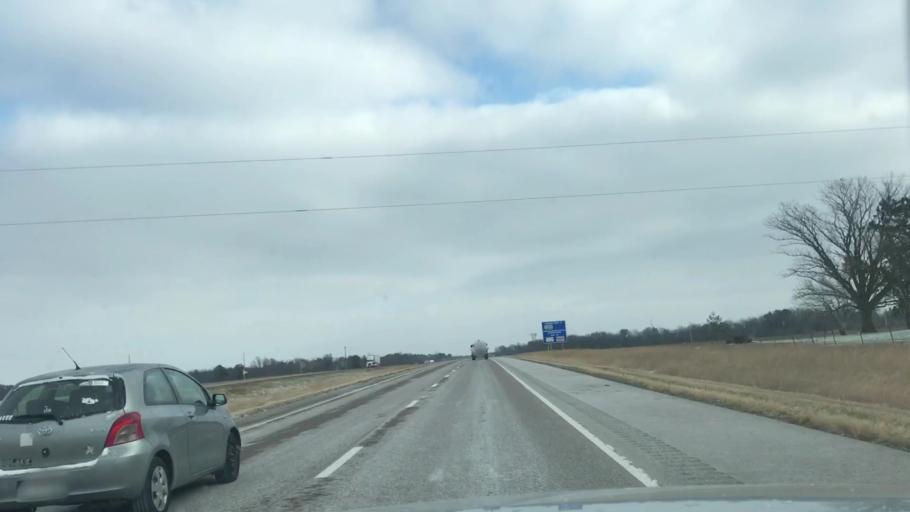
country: US
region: Illinois
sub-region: Madison County
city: Worden
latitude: 38.9491
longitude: -89.7776
